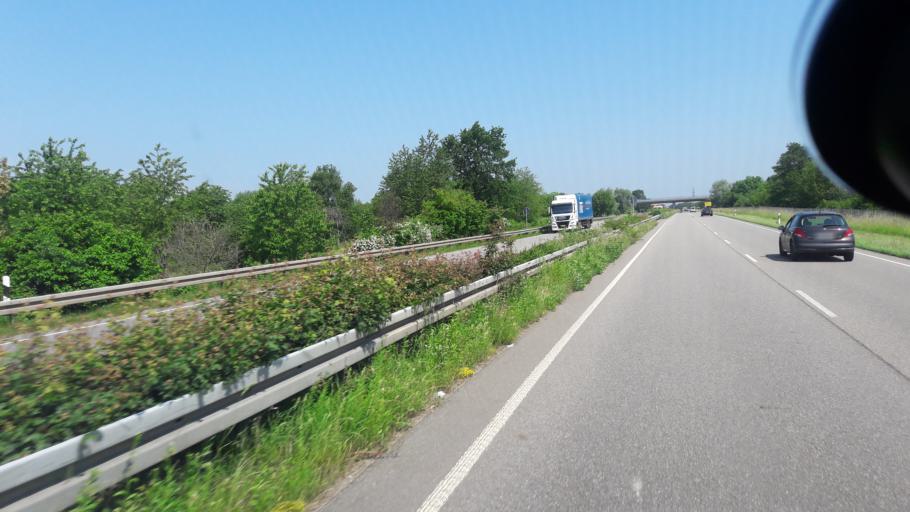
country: DE
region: Baden-Wuerttemberg
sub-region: Karlsruhe Region
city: Bischweier
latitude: 48.8373
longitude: 8.2680
